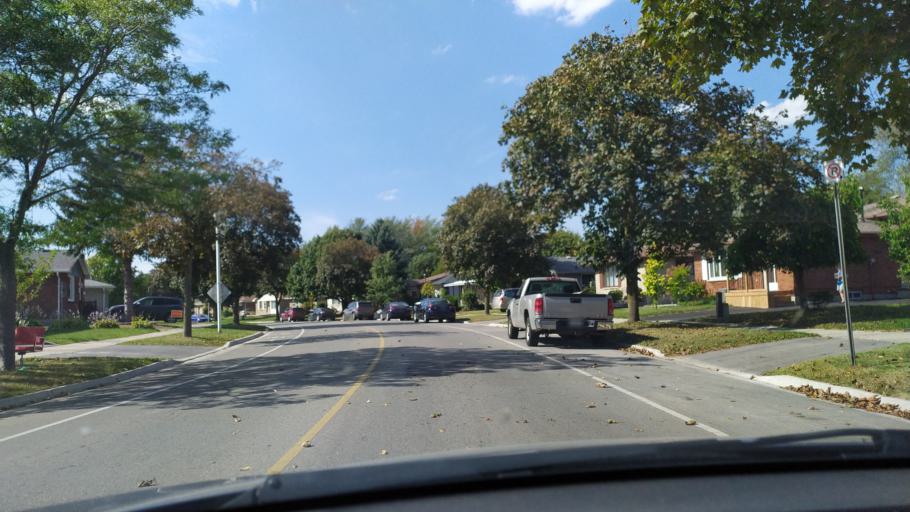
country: CA
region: Ontario
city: London
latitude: 42.9469
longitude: -81.2441
